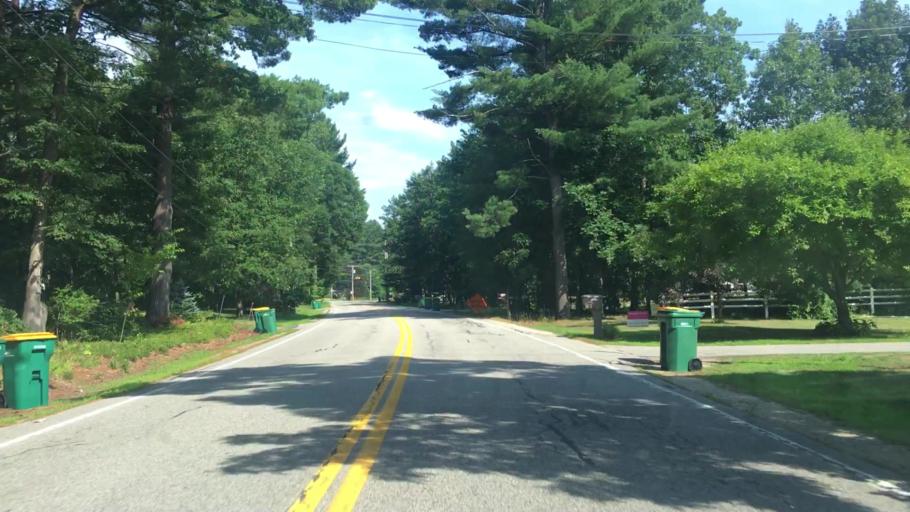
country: US
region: New Hampshire
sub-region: Strafford County
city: Rochester
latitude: 43.2729
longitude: -70.9554
